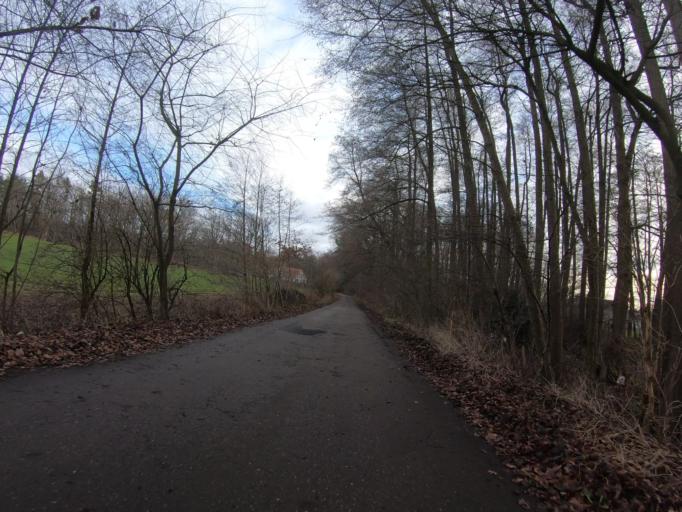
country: DE
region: Lower Saxony
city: Gifhorn
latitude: 52.4895
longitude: 10.5191
